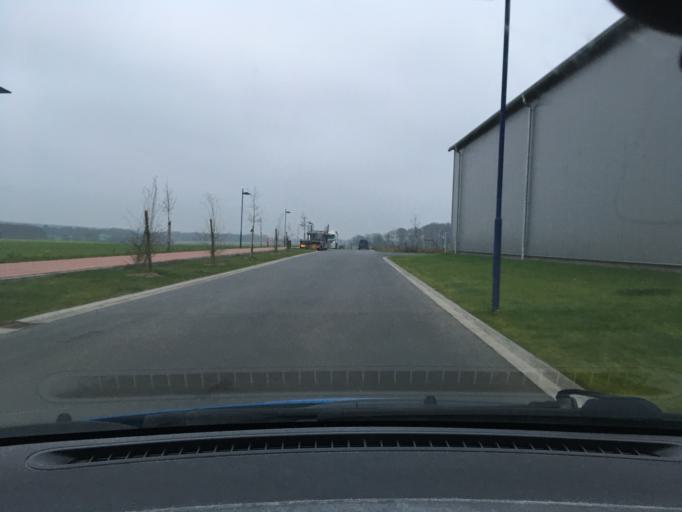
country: DE
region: Lower Saxony
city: Bispingen
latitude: 53.1001
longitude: 9.9810
